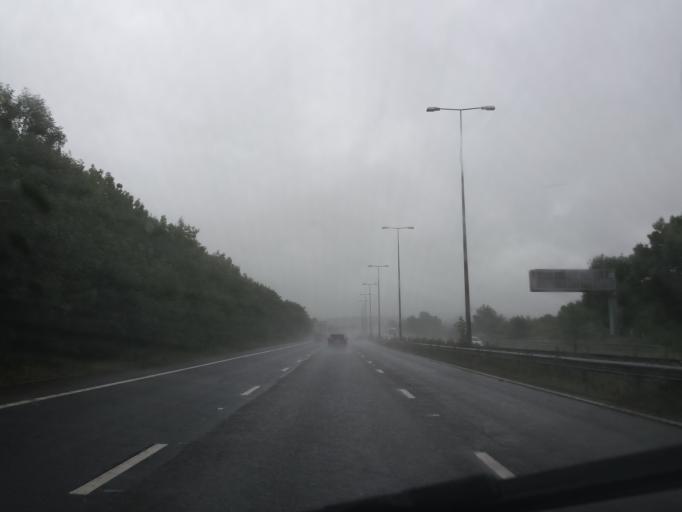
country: GB
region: England
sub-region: Leicestershire
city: Shepshed
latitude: 52.7875
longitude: -1.2864
